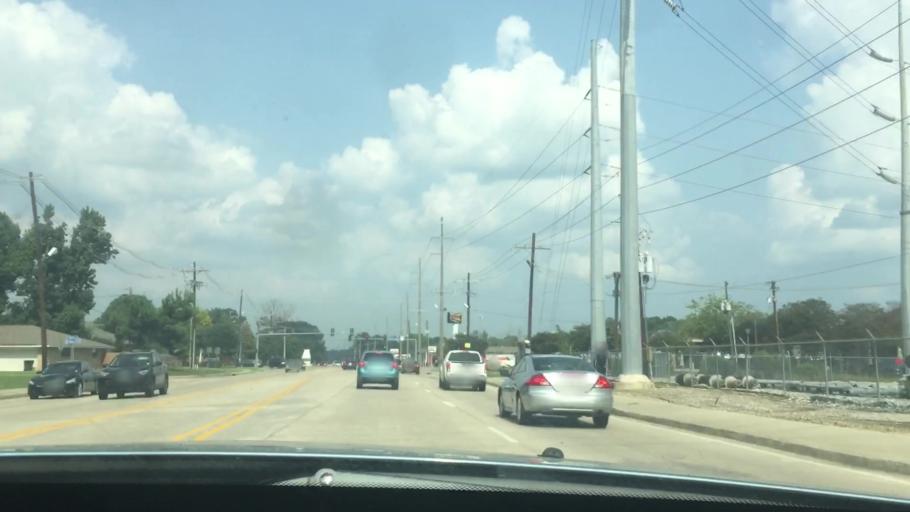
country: US
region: Louisiana
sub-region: East Baton Rouge Parish
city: Westminster
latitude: 30.4356
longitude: -91.0619
